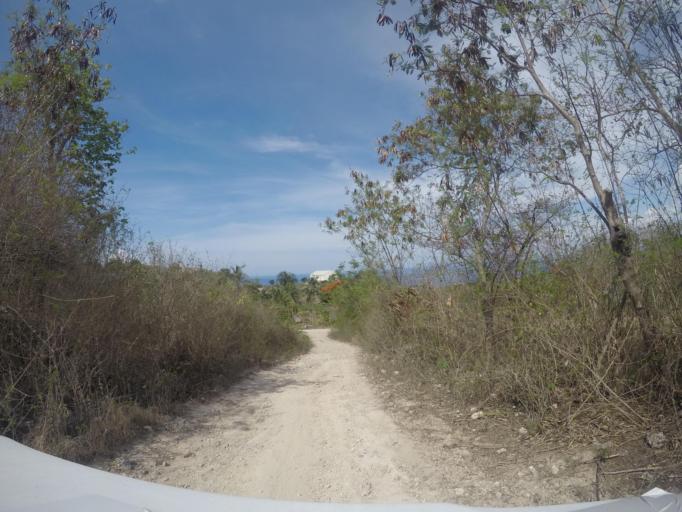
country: TL
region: Baucau
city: Baucau
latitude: -8.4667
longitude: 126.4706
